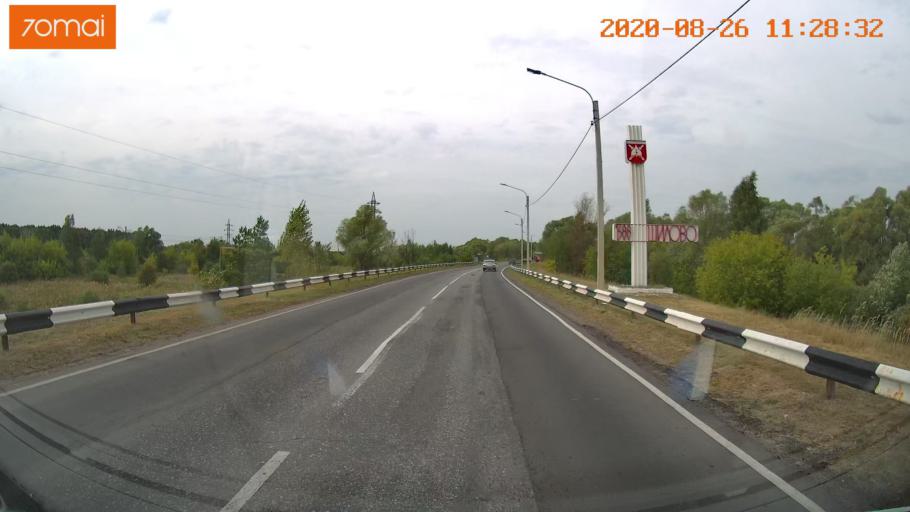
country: RU
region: Rjazan
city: Shilovo
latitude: 54.3232
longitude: 40.9109
